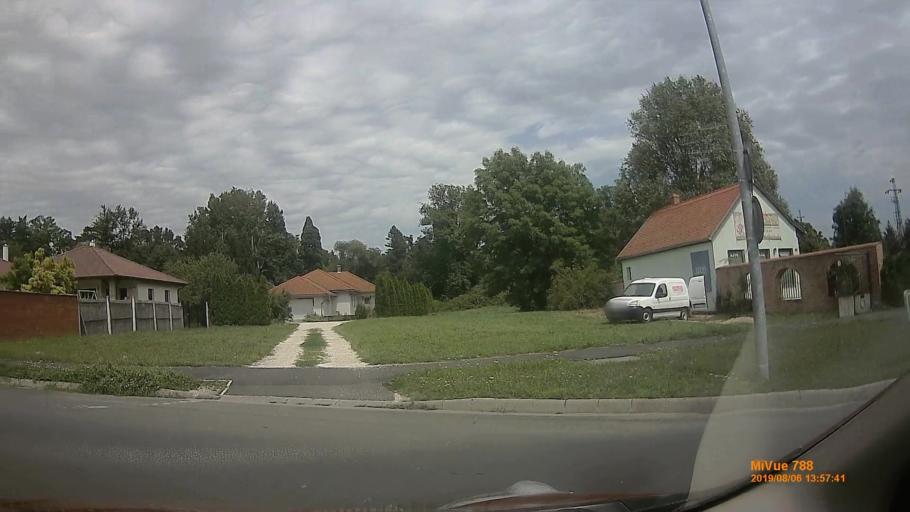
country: HU
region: Vas
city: Szombathely
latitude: 47.2504
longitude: 16.6075
